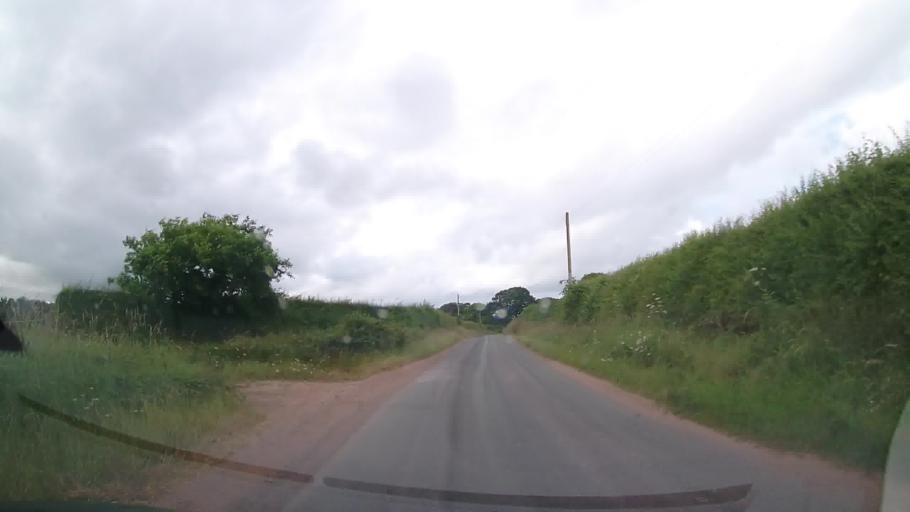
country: GB
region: England
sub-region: Shropshire
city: Whitchurch
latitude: 52.9295
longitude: -2.7319
